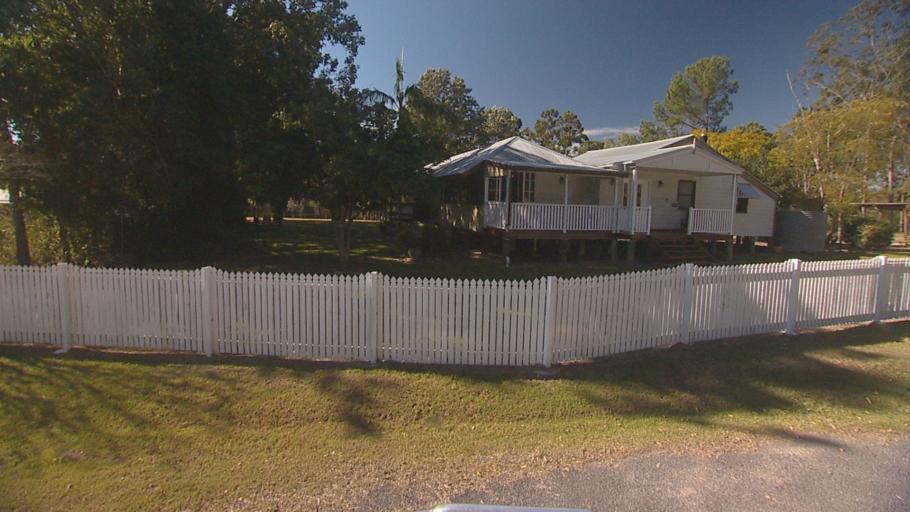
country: AU
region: Queensland
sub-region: Ipswich
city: Springfield Lakes
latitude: -27.7254
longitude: 152.9492
